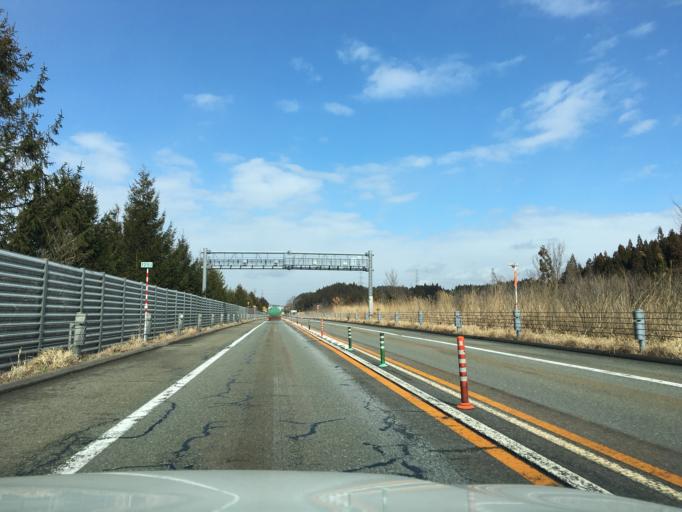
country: JP
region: Akita
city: Akita Shi
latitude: 39.8007
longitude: 140.0984
